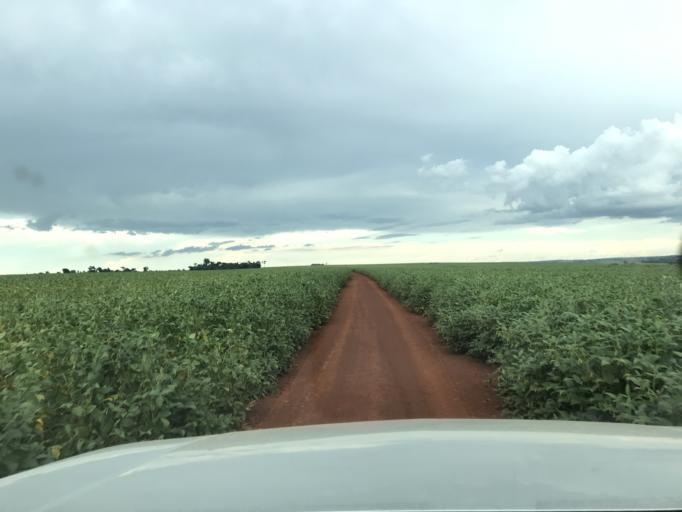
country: BR
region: Parana
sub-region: Palotina
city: Palotina
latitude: -24.2703
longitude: -53.7808
